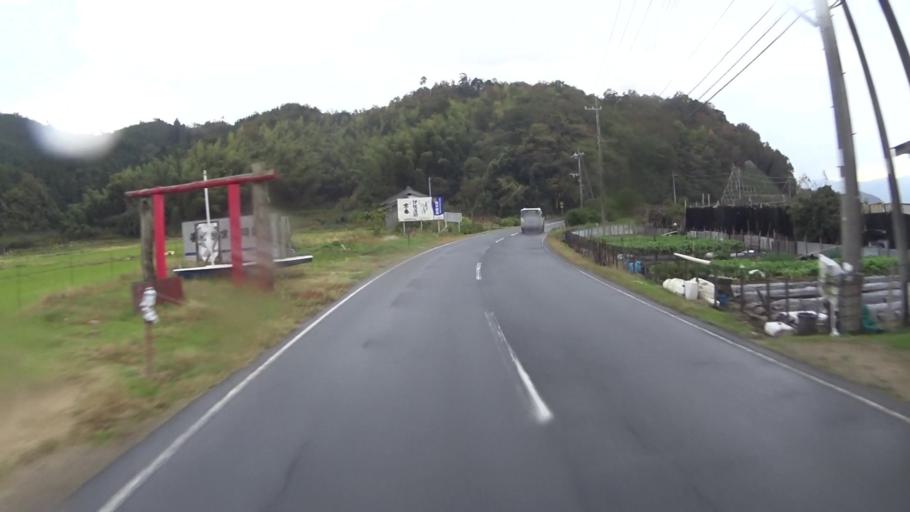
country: JP
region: Kyoto
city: Miyazu
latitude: 35.5771
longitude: 135.2304
